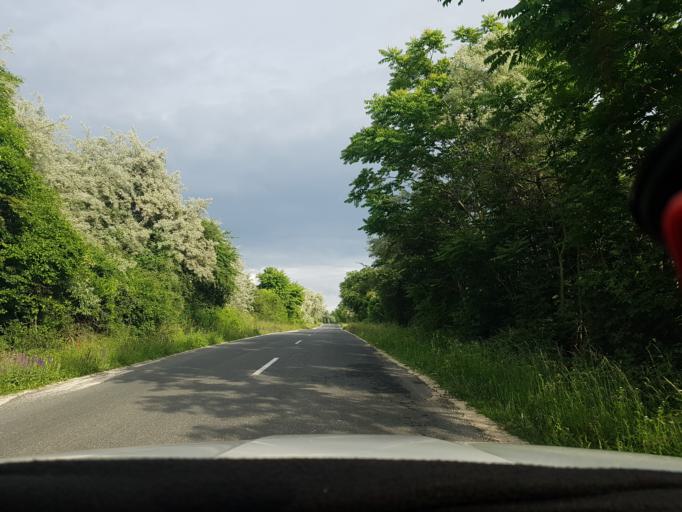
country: HU
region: Komarom-Esztergom
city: Labatlan
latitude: 47.7296
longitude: 18.5313
